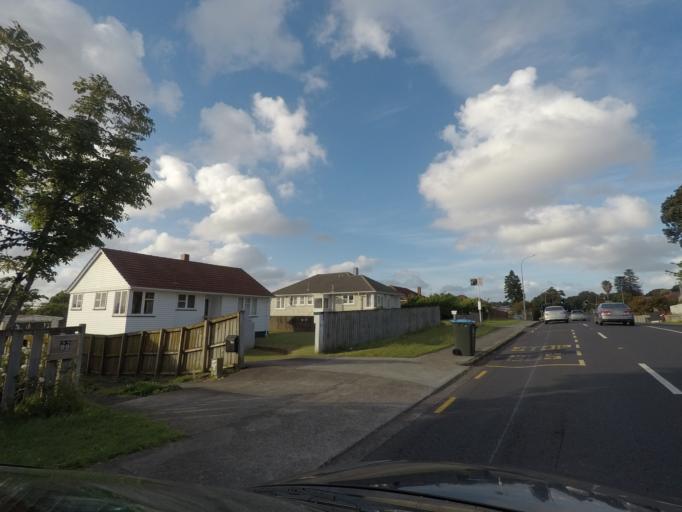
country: NZ
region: Auckland
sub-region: Auckland
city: Auckland
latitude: -36.9165
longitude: 174.7587
